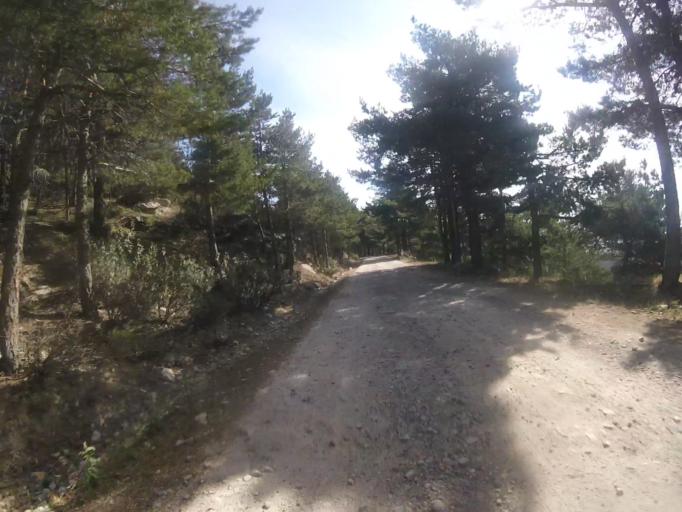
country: ES
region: Madrid
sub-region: Provincia de Madrid
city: Guadarrama
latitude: 40.6923
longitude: -4.1502
